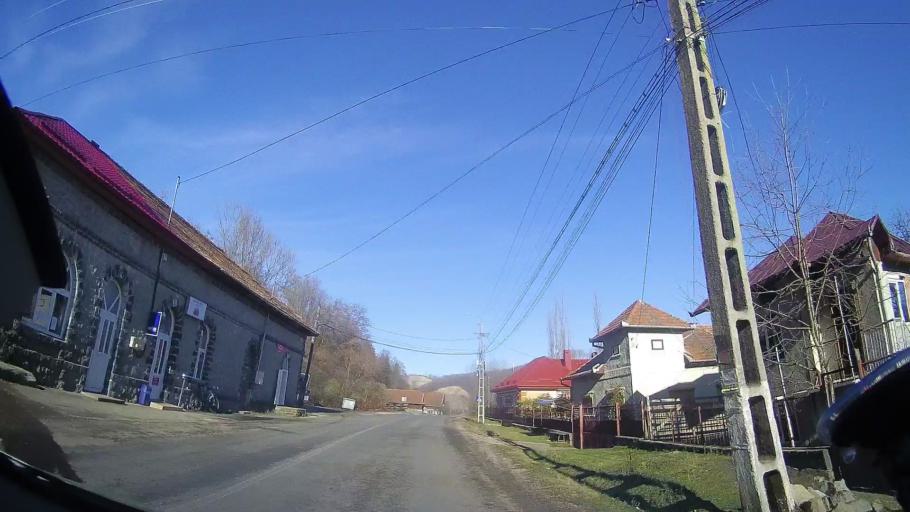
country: RO
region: Cluj
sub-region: Comuna Poeni
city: Poeni
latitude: 46.8818
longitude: 22.8787
